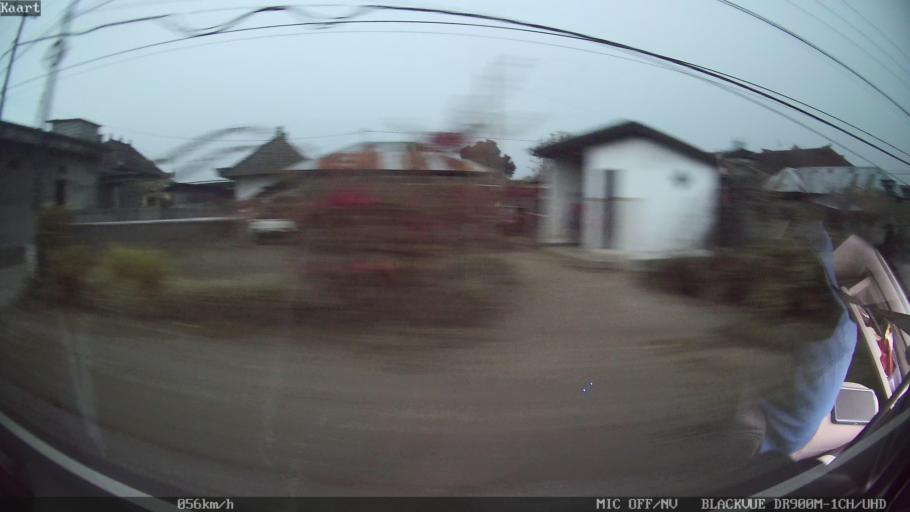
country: ID
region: Bali
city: Banjar Kedisan
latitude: -8.2891
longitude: 115.3185
